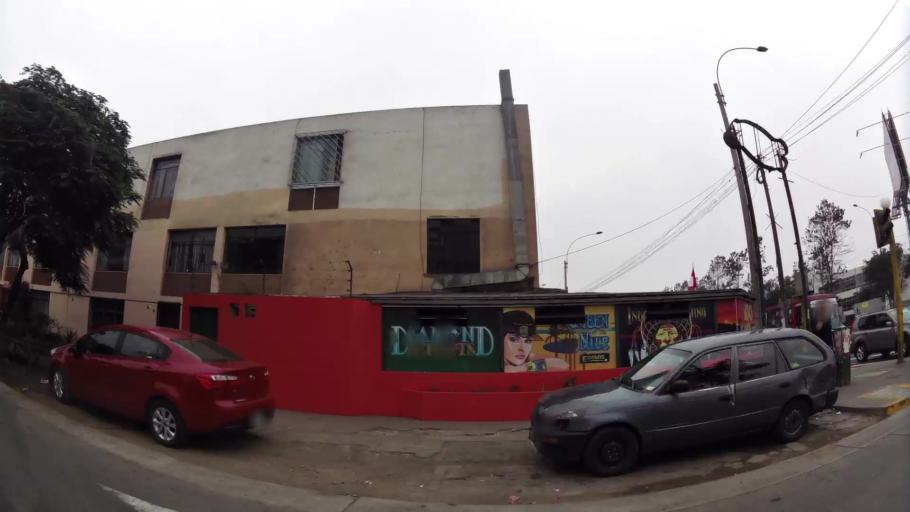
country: PE
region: Lima
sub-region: Lima
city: San Luis
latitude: -12.0817
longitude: -77.0216
